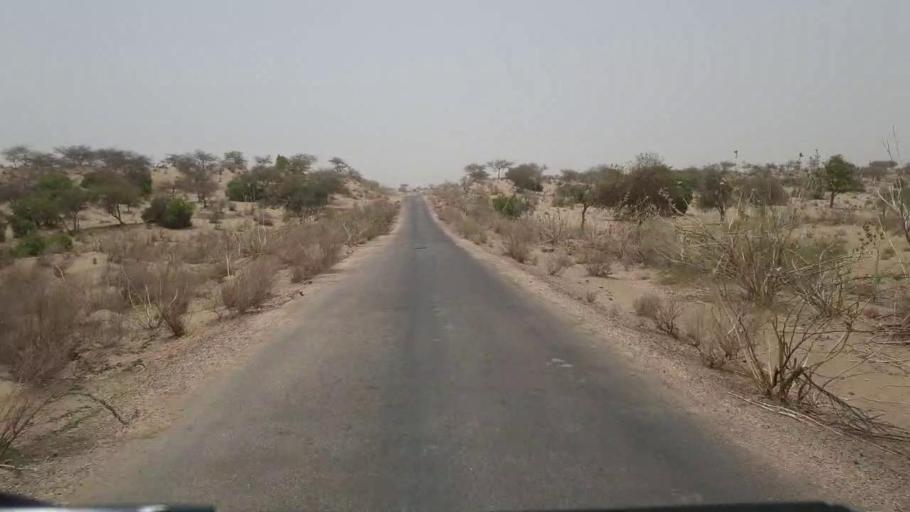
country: PK
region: Sindh
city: Naukot
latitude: 24.7737
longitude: 69.5371
